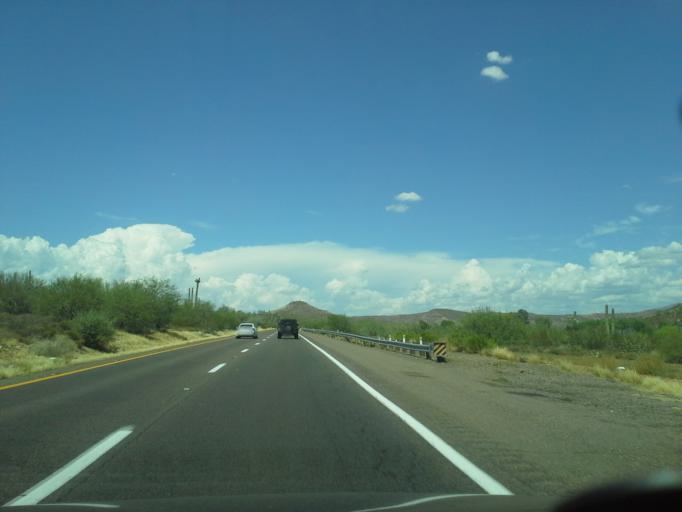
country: US
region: Arizona
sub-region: Maricopa County
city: New River
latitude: 33.9484
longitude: -112.1375
